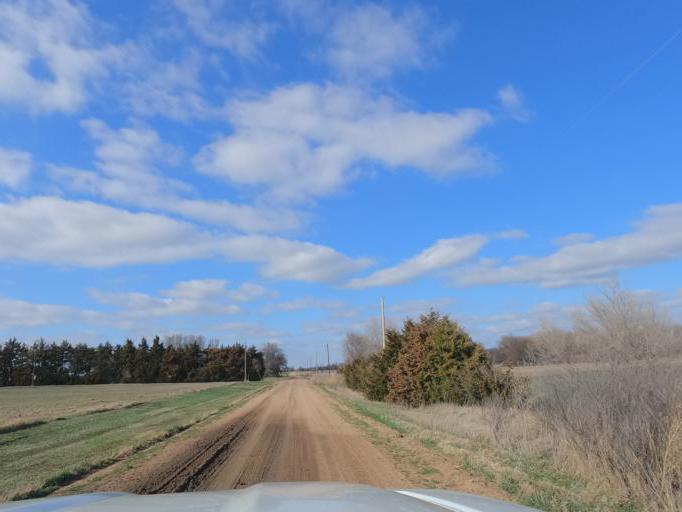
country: US
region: Kansas
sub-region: McPherson County
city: Inman
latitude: 38.2384
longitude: -97.8670
